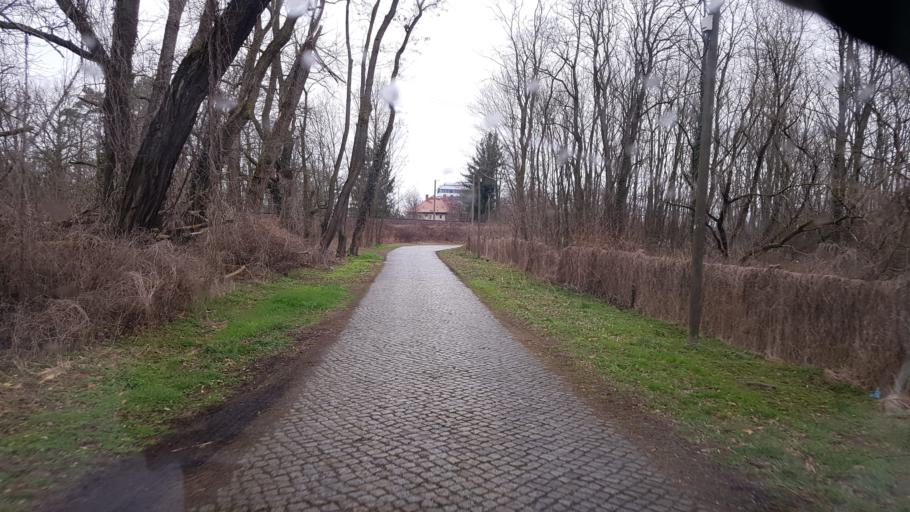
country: DE
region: Brandenburg
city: Ruhland
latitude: 51.4489
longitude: 13.8614
